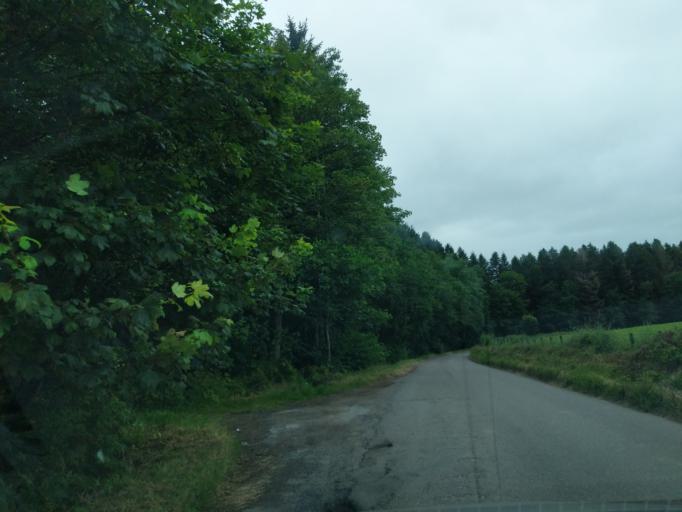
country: GB
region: Scotland
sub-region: Moray
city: Rothes
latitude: 57.4770
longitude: -3.1926
